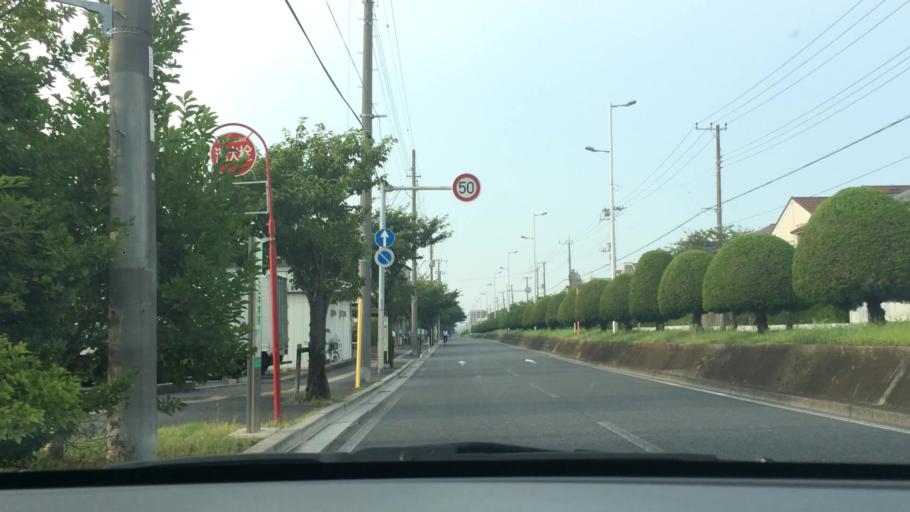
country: JP
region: Tokyo
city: Urayasu
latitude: 35.6399
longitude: 139.8887
